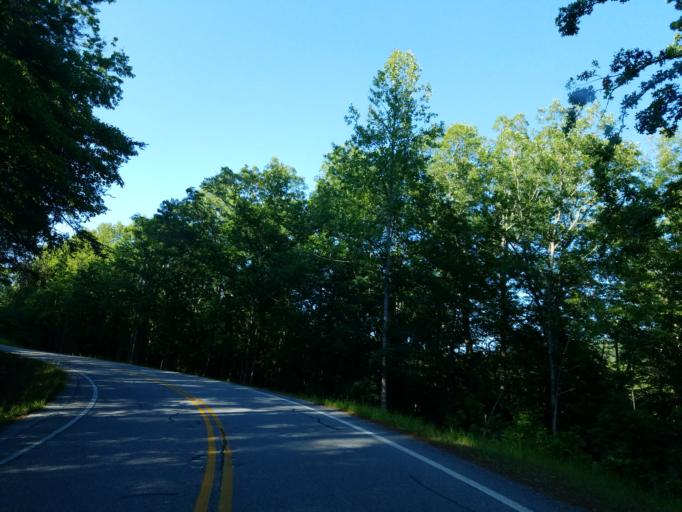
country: US
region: Georgia
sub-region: Fannin County
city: Blue Ridge
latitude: 34.8028
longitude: -84.1860
